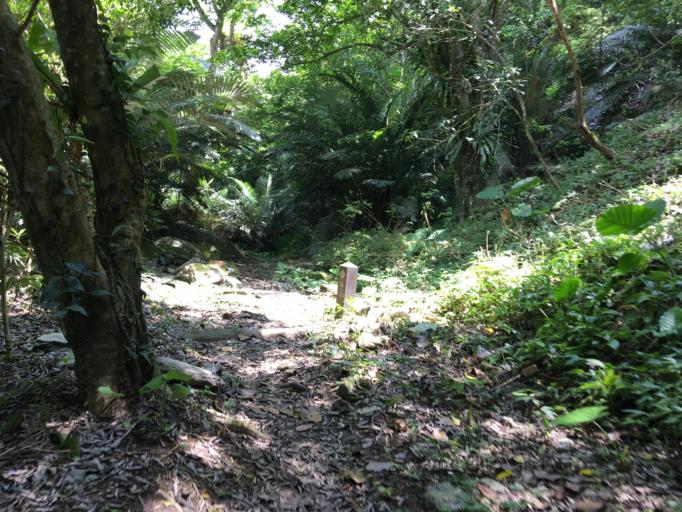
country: TW
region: Taiwan
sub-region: Yilan
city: Yilan
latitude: 24.4283
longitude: 121.6939
